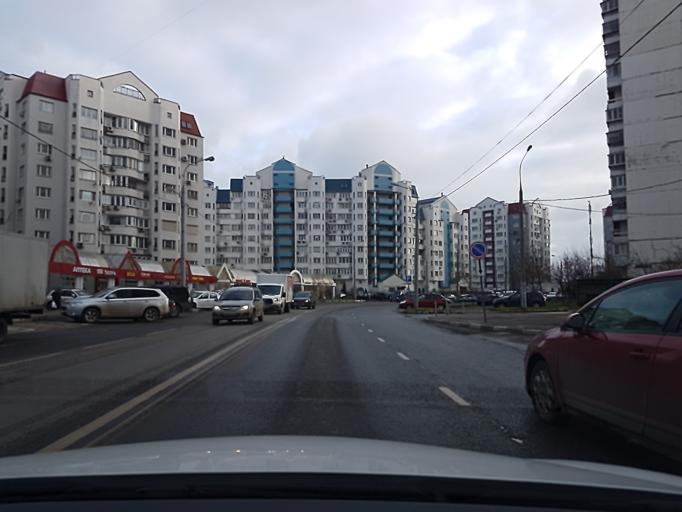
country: RU
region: Moskovskaya
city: Pavshino
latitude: 55.8357
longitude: 37.3562
